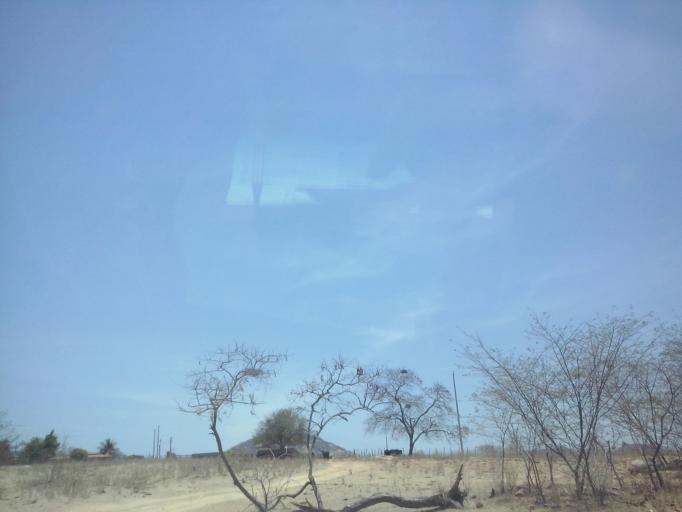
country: BR
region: Paraiba
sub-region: Paulista
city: Paulista
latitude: -6.5971
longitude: -37.6610
